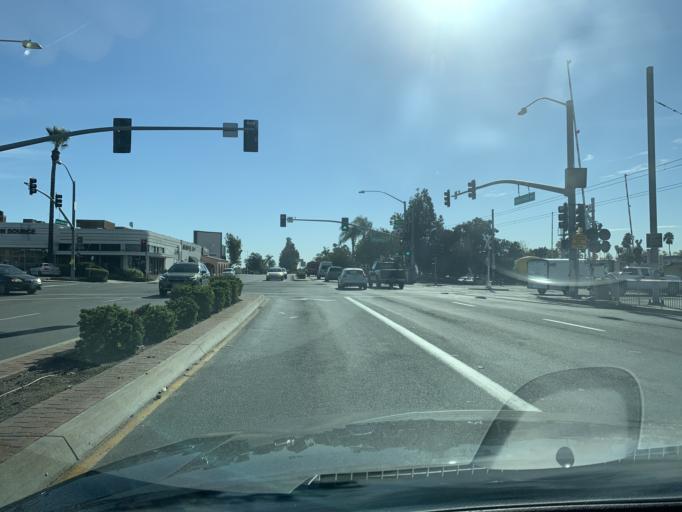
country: US
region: California
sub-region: San Diego County
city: Lemon Grove
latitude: 32.7431
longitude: -117.0306
